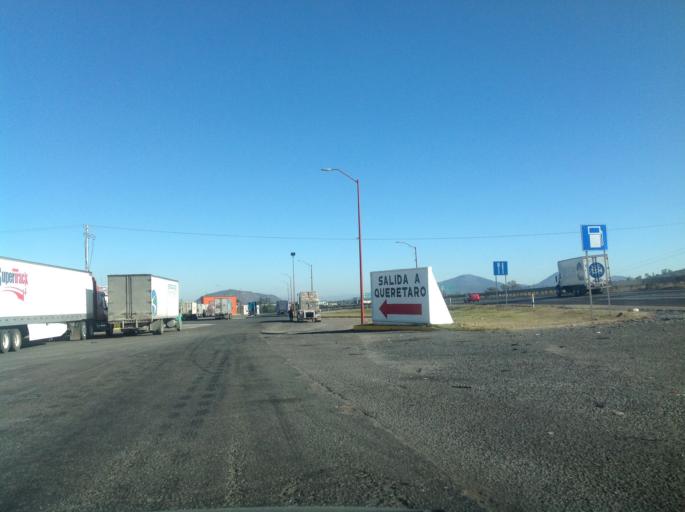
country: MX
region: Queretaro
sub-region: San Juan del Rio
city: Paso de Mata
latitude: 20.3136
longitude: -99.9315
